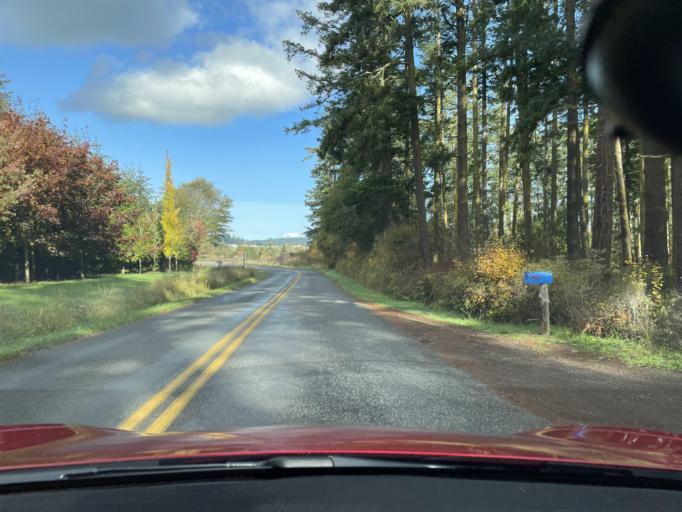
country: US
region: Washington
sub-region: San Juan County
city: Friday Harbor
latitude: 48.5101
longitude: -123.0232
